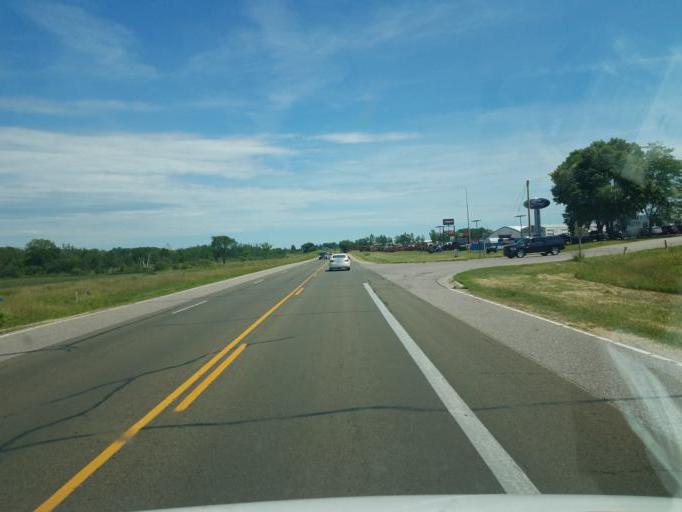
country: US
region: Wisconsin
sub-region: Sauk County
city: Reedsburg
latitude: 43.5475
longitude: -90.0542
